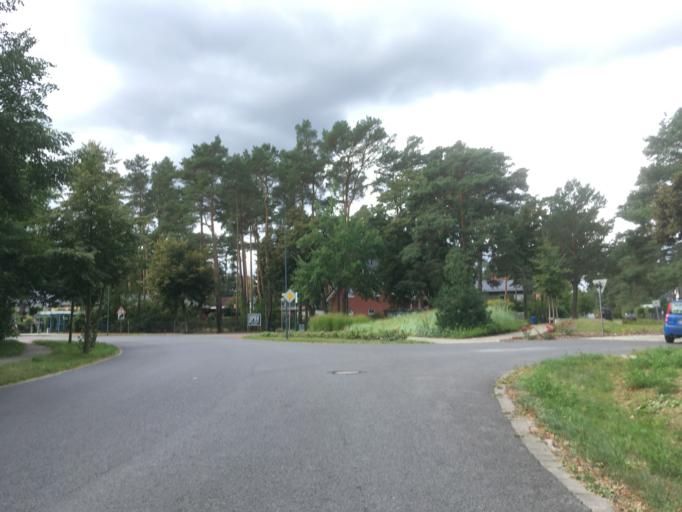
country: DE
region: Brandenburg
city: Wildau
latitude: 52.3151
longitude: 13.7024
